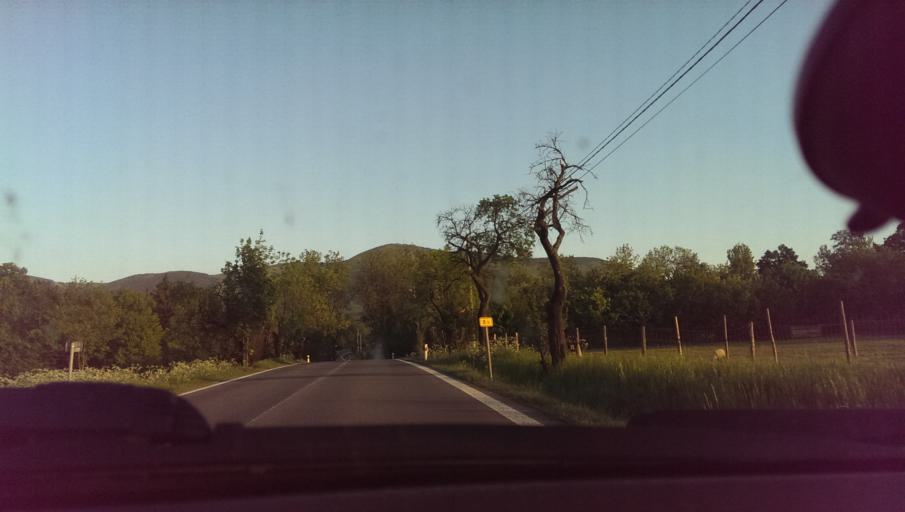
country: CZ
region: Moravskoslezsky
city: Frenstat pod Radhostem
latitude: 49.5316
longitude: 18.2033
